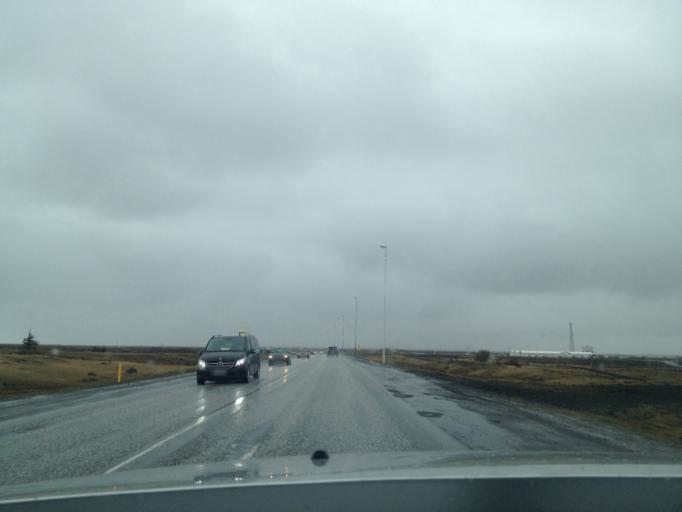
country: IS
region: Southern Peninsula
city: Reykjanesbaer
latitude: 63.9927
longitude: -22.5815
